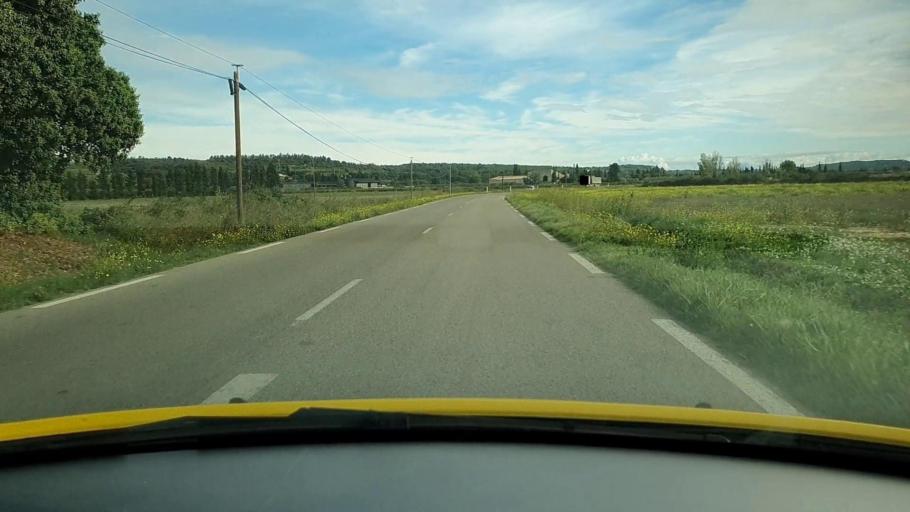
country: FR
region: Languedoc-Roussillon
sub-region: Departement du Gard
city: Jonquieres-Saint-Vincent
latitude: 43.7905
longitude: 4.5815
